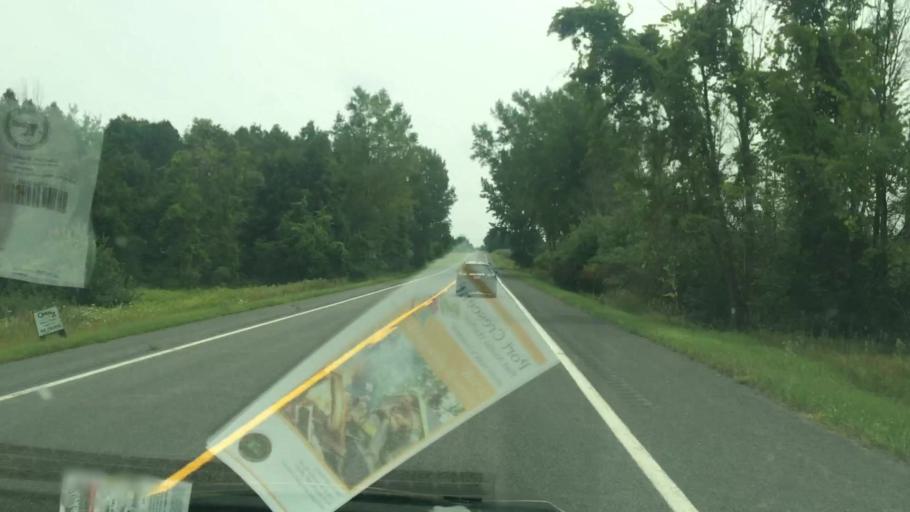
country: US
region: Michigan
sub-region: Huron County
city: Harbor Beach
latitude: 44.0183
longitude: -82.8044
